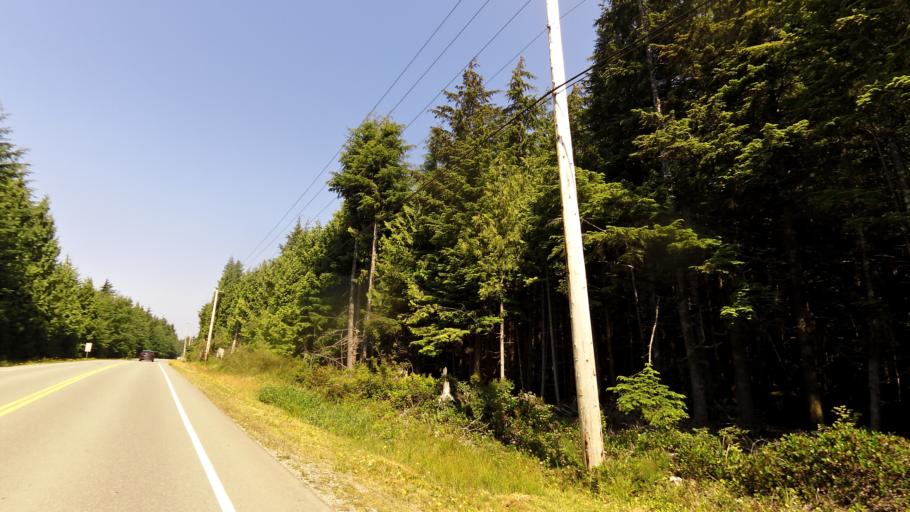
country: CA
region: British Columbia
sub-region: Regional District of Alberni-Clayoquot
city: Ucluelet
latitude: 49.0224
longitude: -125.6403
